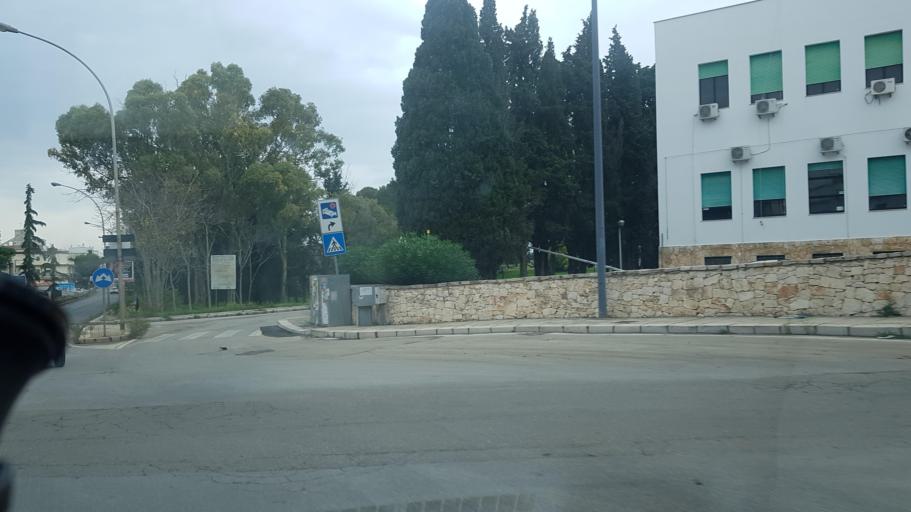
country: IT
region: Apulia
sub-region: Provincia di Brindisi
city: Carovigno
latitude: 40.7051
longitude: 17.6527
